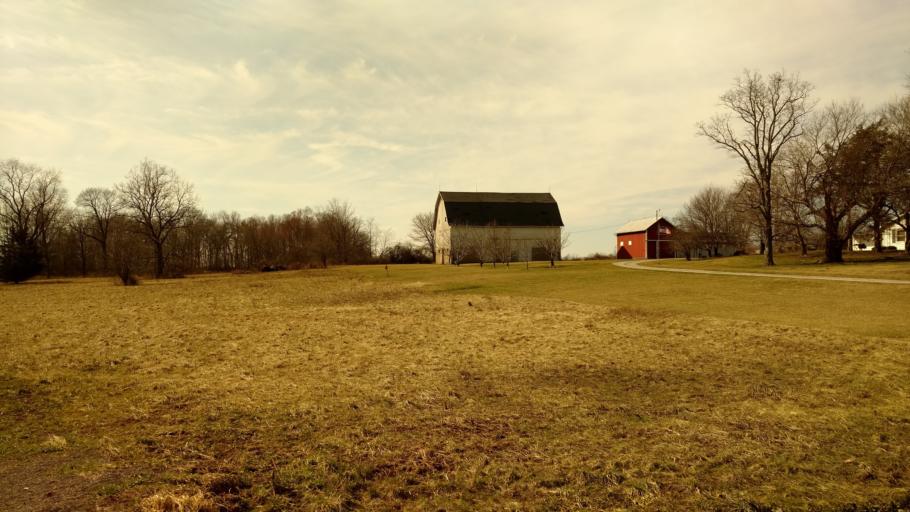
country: US
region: Ohio
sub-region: Hardin County
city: Kenton
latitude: 40.5700
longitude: -83.4685
